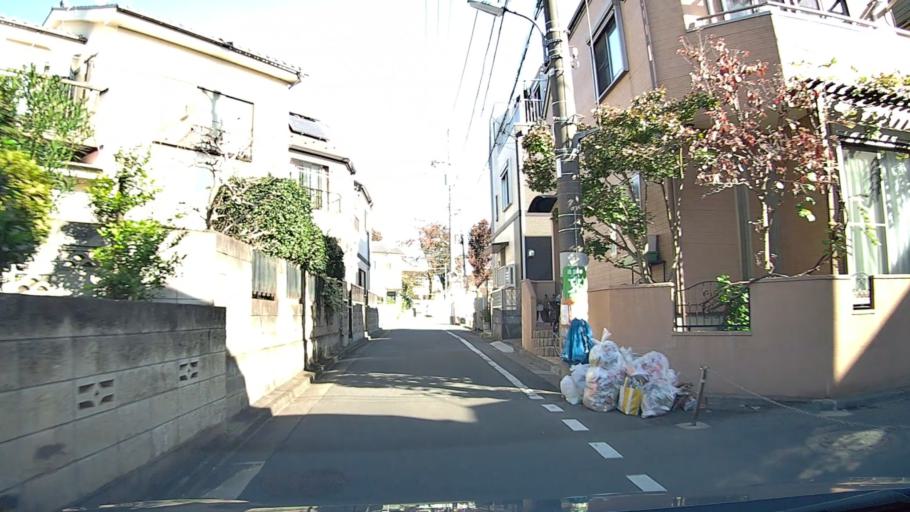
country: JP
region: Saitama
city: Wako
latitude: 35.7401
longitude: 139.6310
